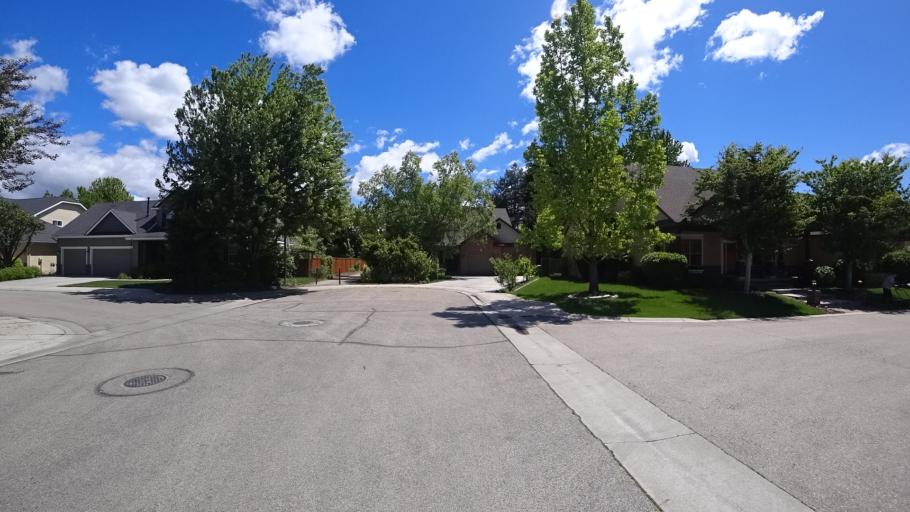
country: US
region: Idaho
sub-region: Ada County
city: Eagle
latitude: 43.6429
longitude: -116.3432
